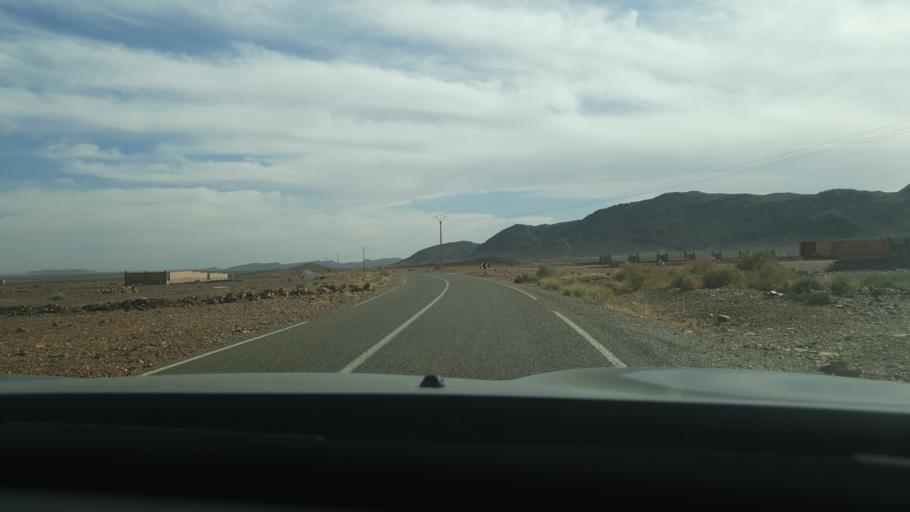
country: MA
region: Meknes-Tafilalet
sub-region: Errachidia
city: Fezna
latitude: 31.5290
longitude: -4.6372
